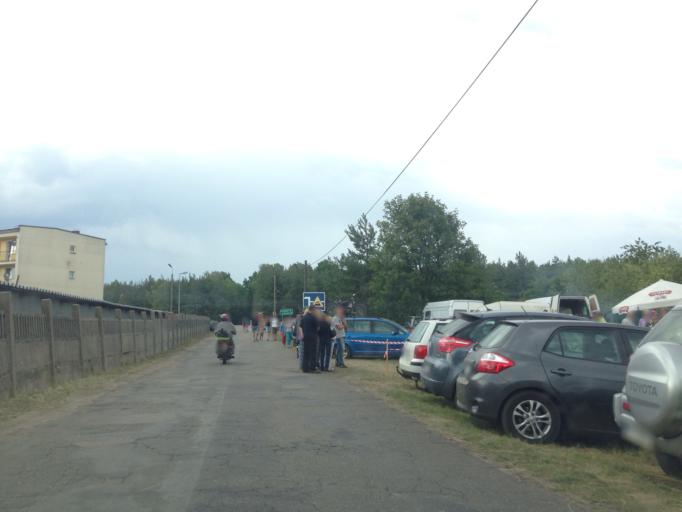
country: PL
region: Kujawsko-Pomorskie
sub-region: Powiat swiecki
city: Lniano
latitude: 53.5434
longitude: 18.1193
